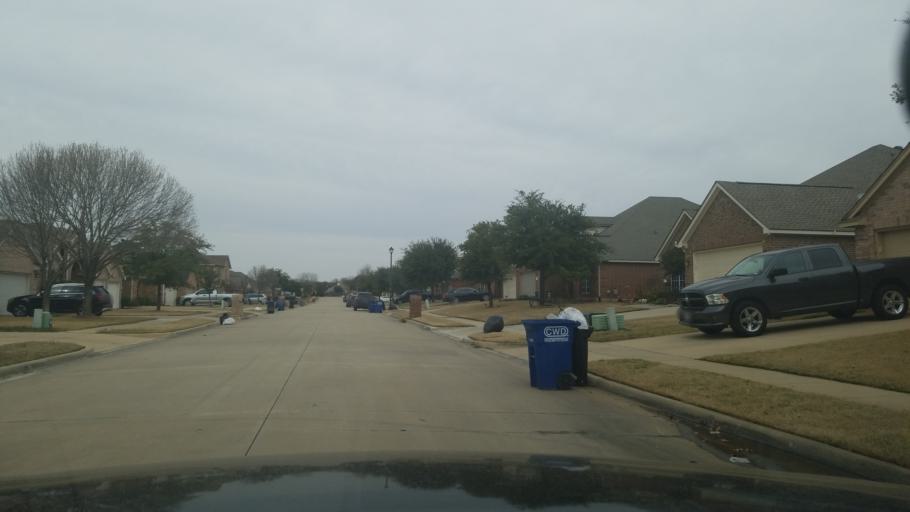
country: US
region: Texas
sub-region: Denton County
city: Corinth
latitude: 33.1323
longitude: -97.0727
